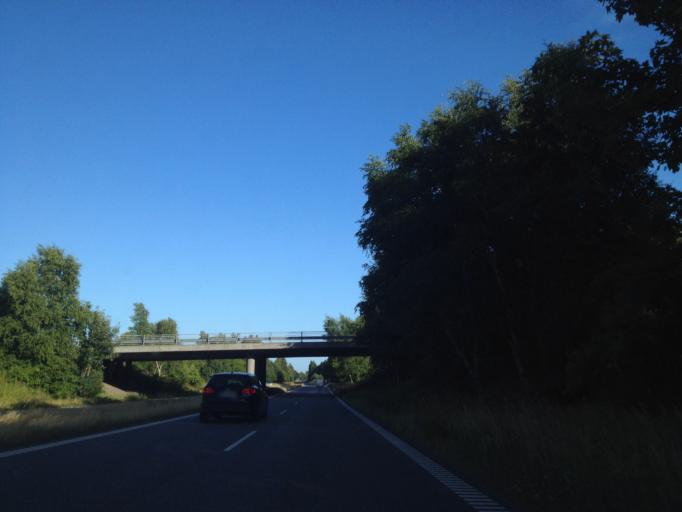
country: DK
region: Capital Region
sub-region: Hillerod Kommune
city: Nodebo
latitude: 55.9359
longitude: 12.3592
